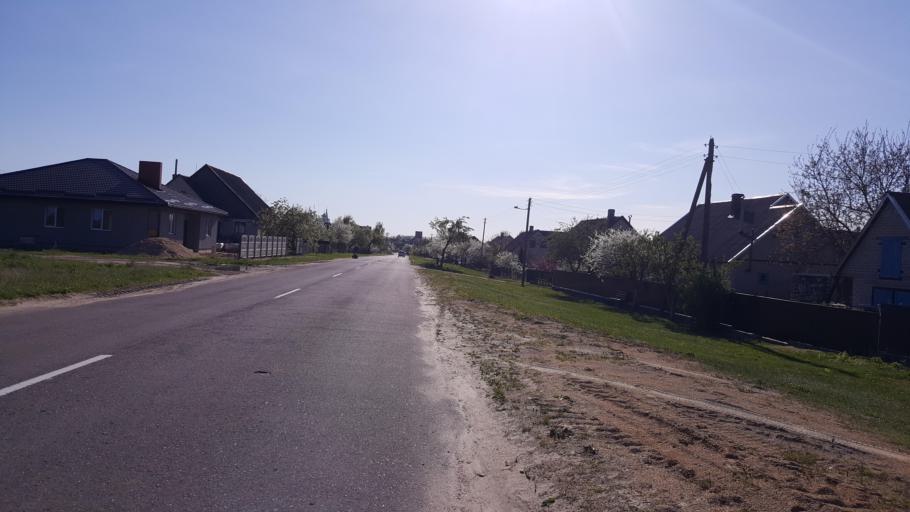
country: BY
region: Brest
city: Kamyanyets
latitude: 52.4082
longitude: 23.8379
